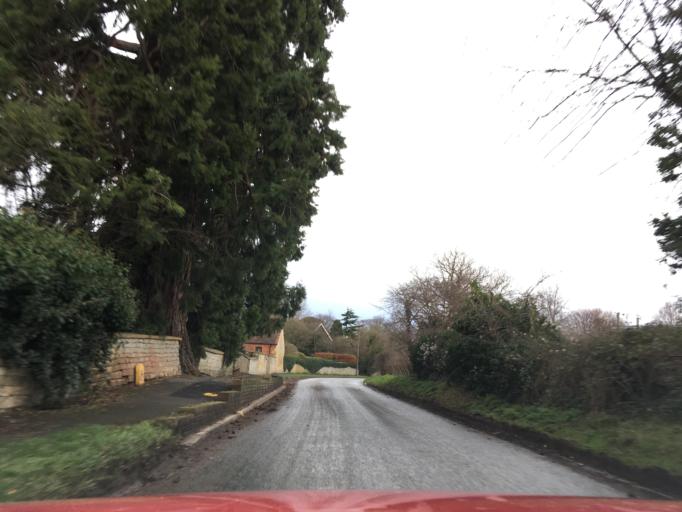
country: GB
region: England
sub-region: Worcestershire
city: Evesham
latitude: 52.0357
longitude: -2.0063
